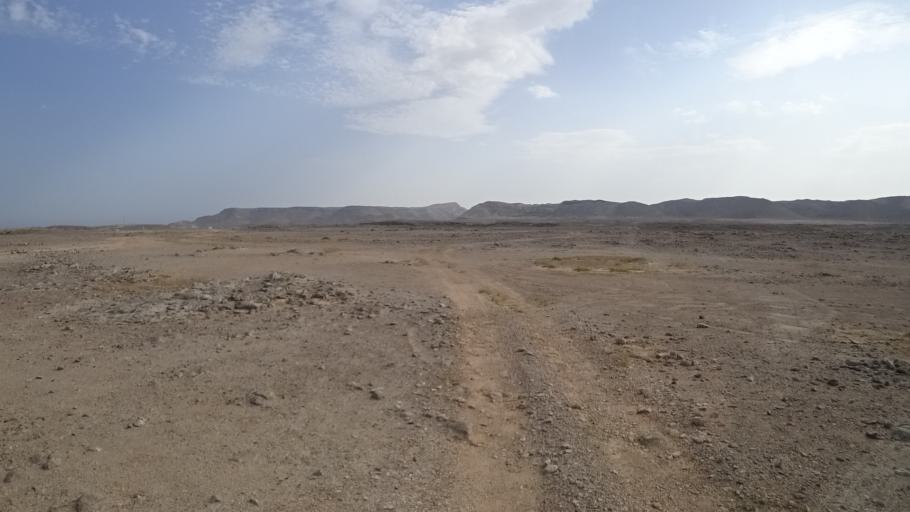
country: OM
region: Ash Sharqiyah
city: Sur
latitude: 22.4557
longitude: 59.8253
